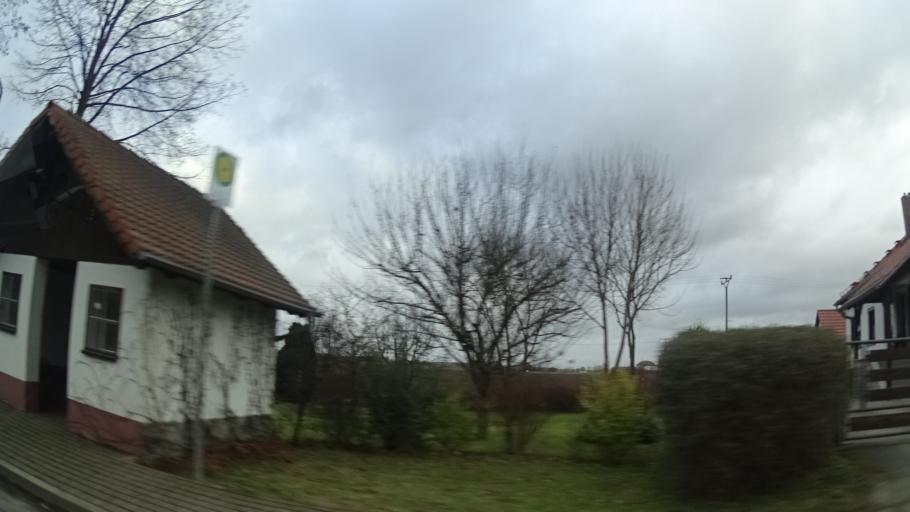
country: DE
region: Thuringia
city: Lemnitz
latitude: 50.7234
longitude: 11.8332
